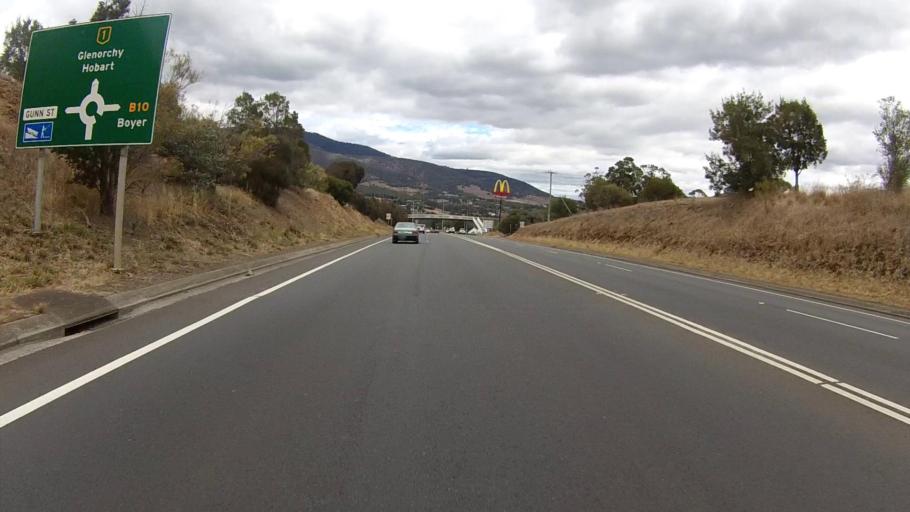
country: AU
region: Tasmania
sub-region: Brighton
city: Bridgewater
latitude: -42.7365
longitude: 147.2306
